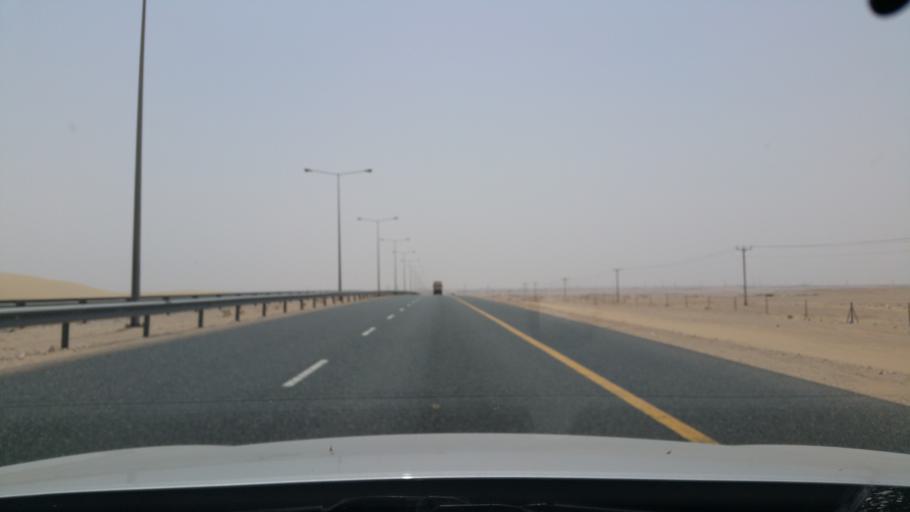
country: QA
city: Umm Bab
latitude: 24.9808
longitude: 50.9413
